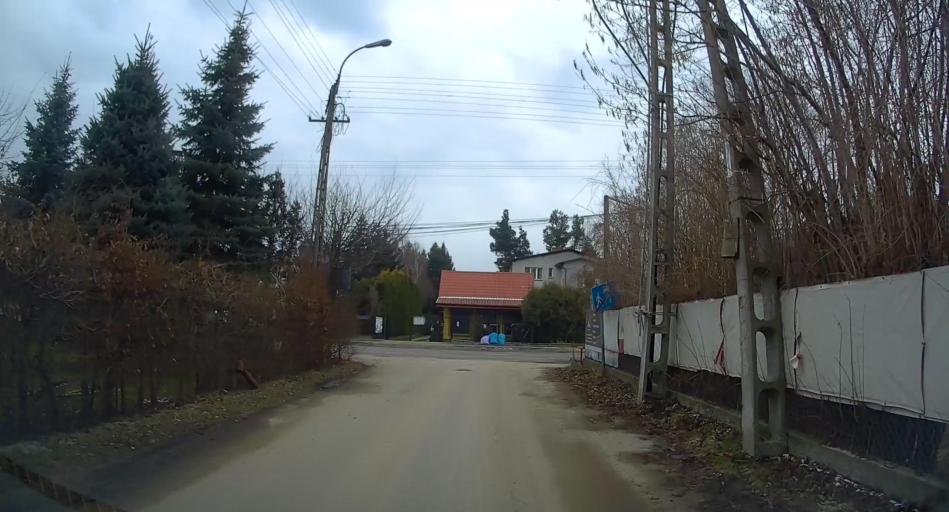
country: PL
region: Masovian Voivodeship
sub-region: Powiat piaseczynski
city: Piaseczno
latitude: 52.0523
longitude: 20.9996
